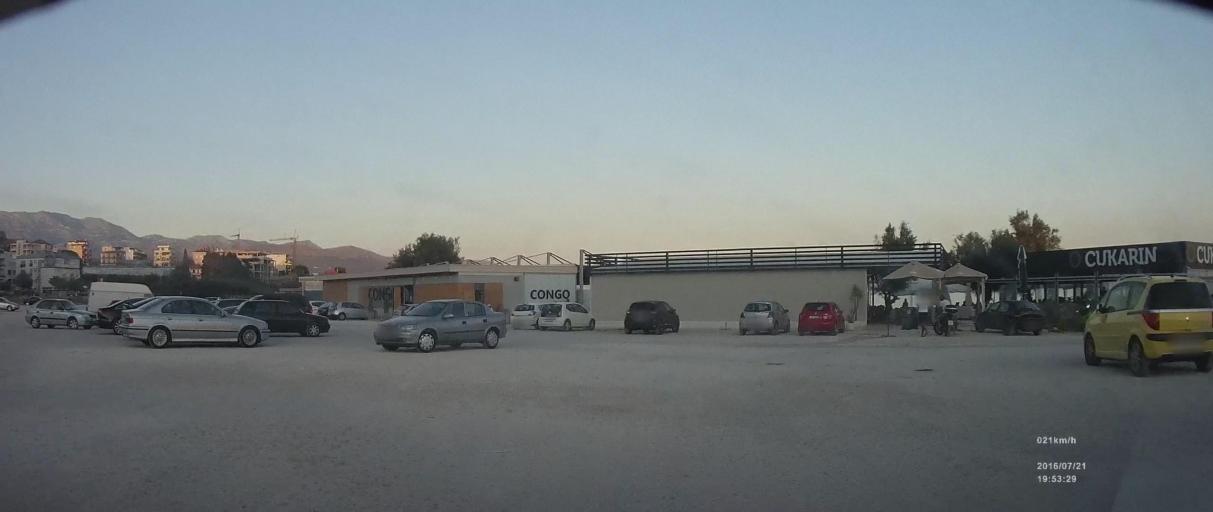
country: HR
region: Splitsko-Dalmatinska
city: Vranjic
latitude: 43.5027
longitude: 16.4769
